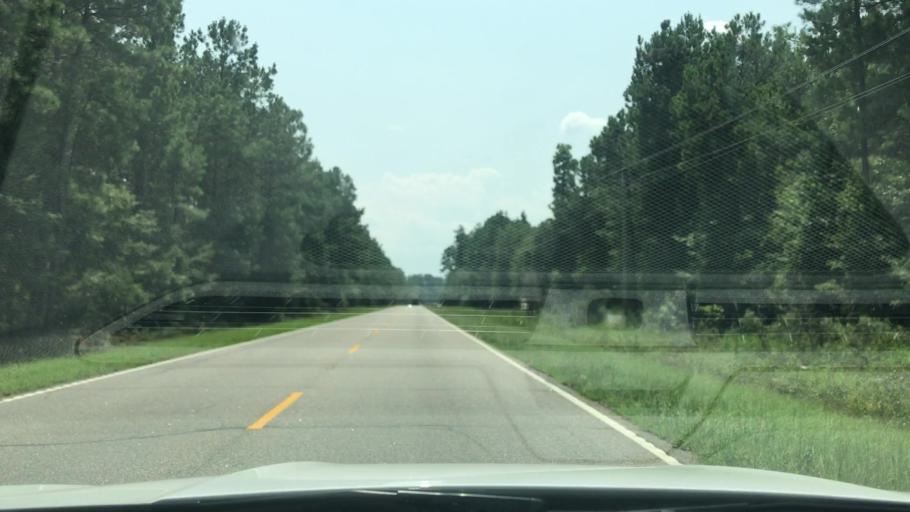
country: US
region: South Carolina
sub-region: Georgetown County
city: Georgetown
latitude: 33.4888
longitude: -79.2657
